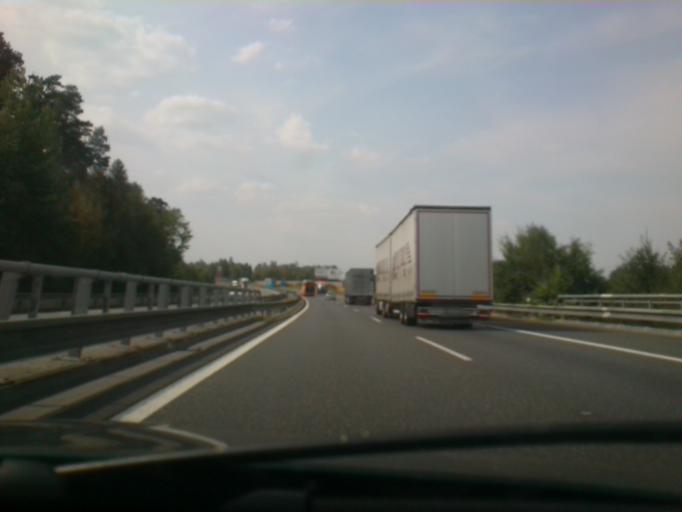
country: CZ
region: Central Bohemia
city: Trhovy Stepanov
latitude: 49.7486
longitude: 15.0282
